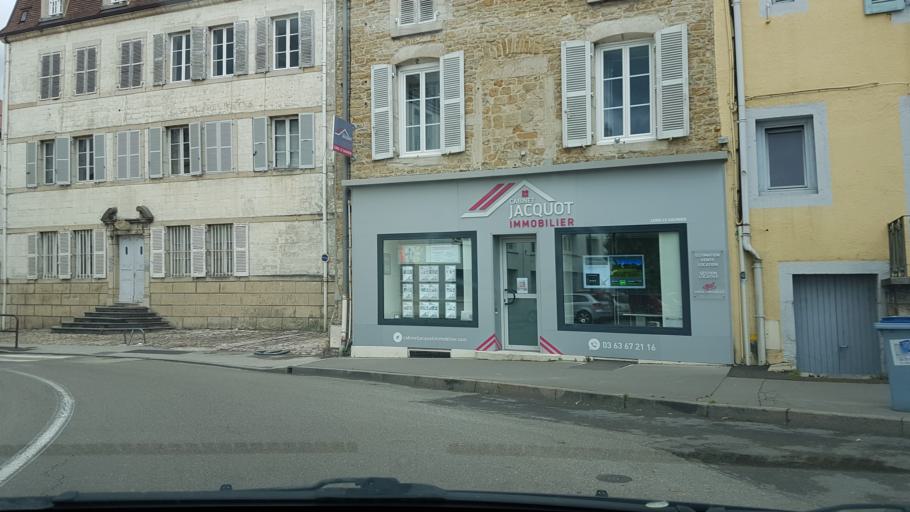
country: FR
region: Franche-Comte
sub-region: Departement du Jura
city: Lons-le-Saunier
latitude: 46.6760
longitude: 5.5548
